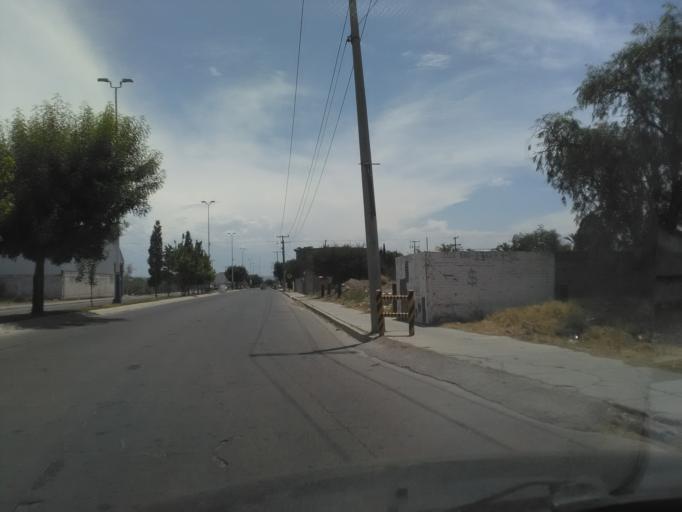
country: MX
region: Durango
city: Victoria de Durango
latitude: 24.0272
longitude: -104.6151
